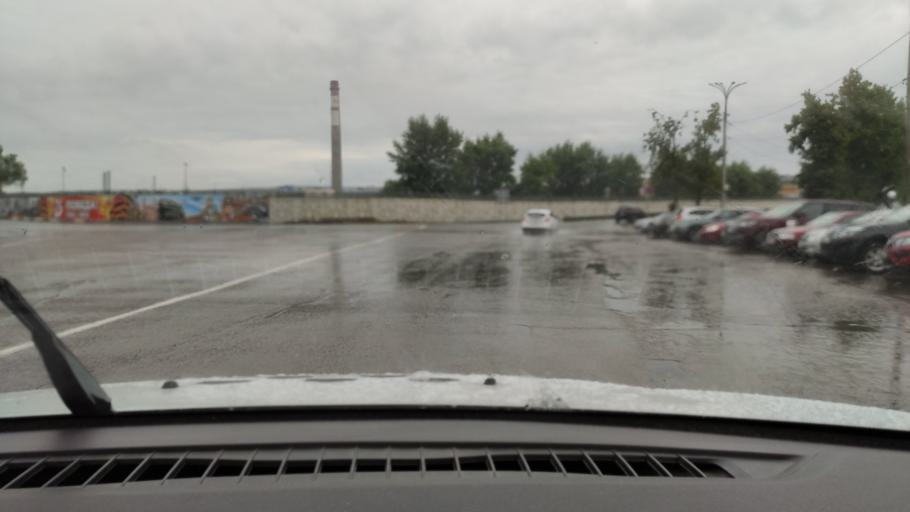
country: RU
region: Udmurtiya
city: Votkinsk
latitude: 57.0525
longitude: 53.9848
